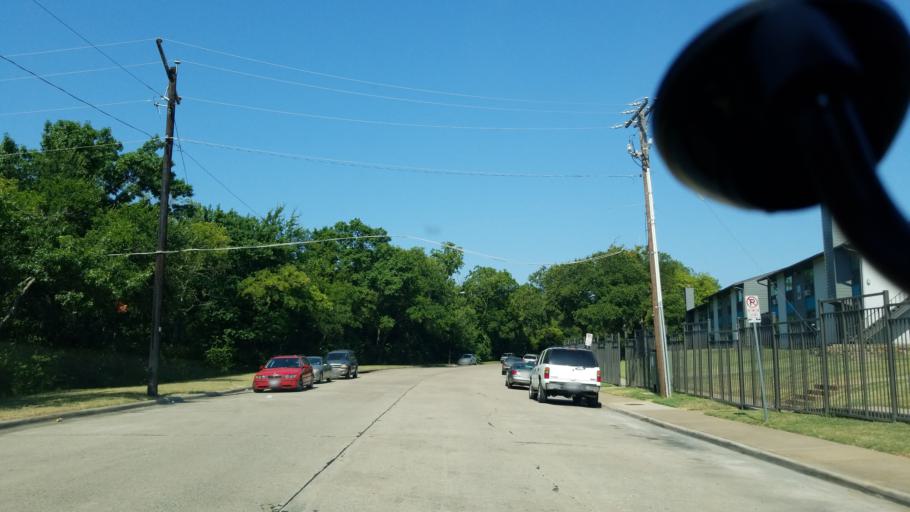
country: US
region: Texas
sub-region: Dallas County
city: Cockrell Hill
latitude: 32.7057
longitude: -96.8679
